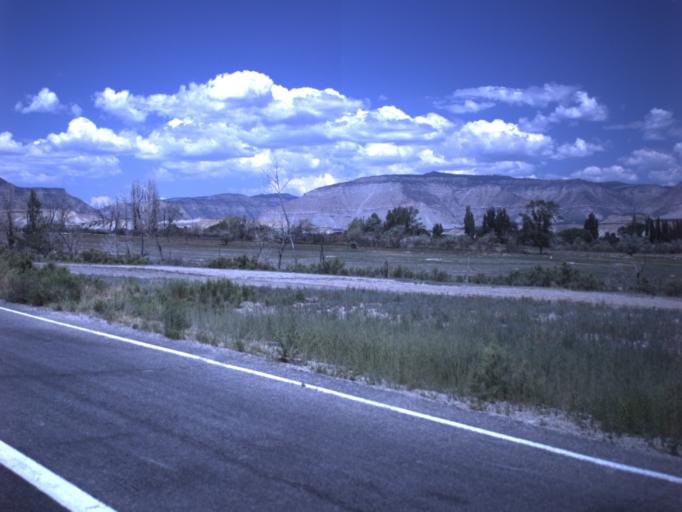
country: US
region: Utah
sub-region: Emery County
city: Orangeville
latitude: 39.2127
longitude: -111.0537
